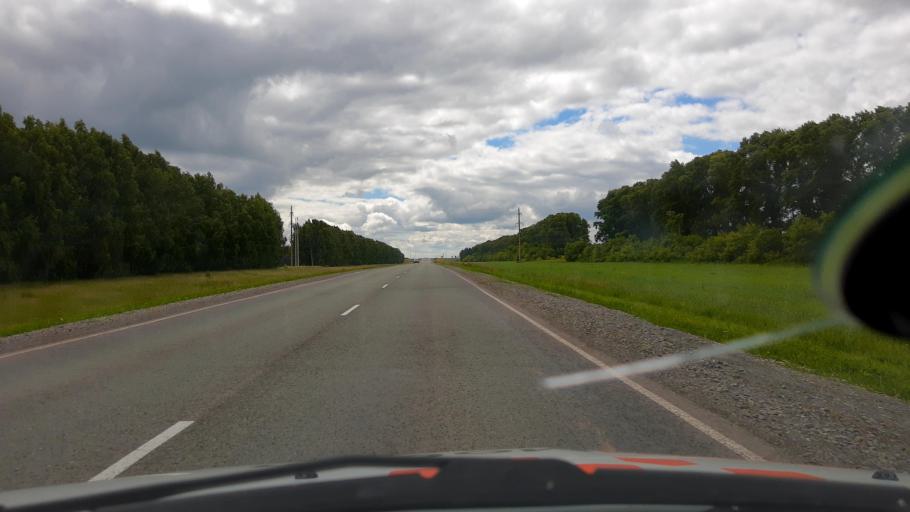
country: RU
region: Bashkortostan
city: Buzdyak
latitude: 54.6584
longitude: 54.5414
